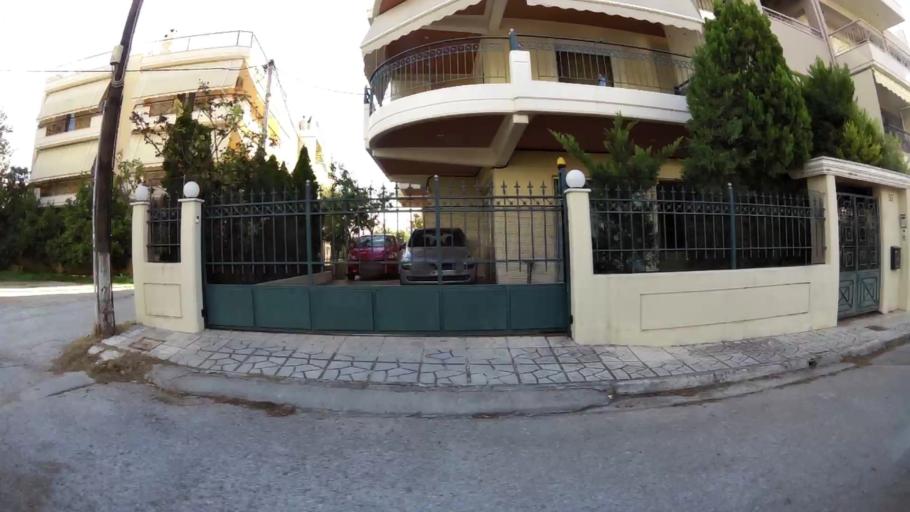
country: GR
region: Attica
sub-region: Nomarchia Anatolikis Attikis
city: Acharnes
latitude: 38.0669
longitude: 23.7428
